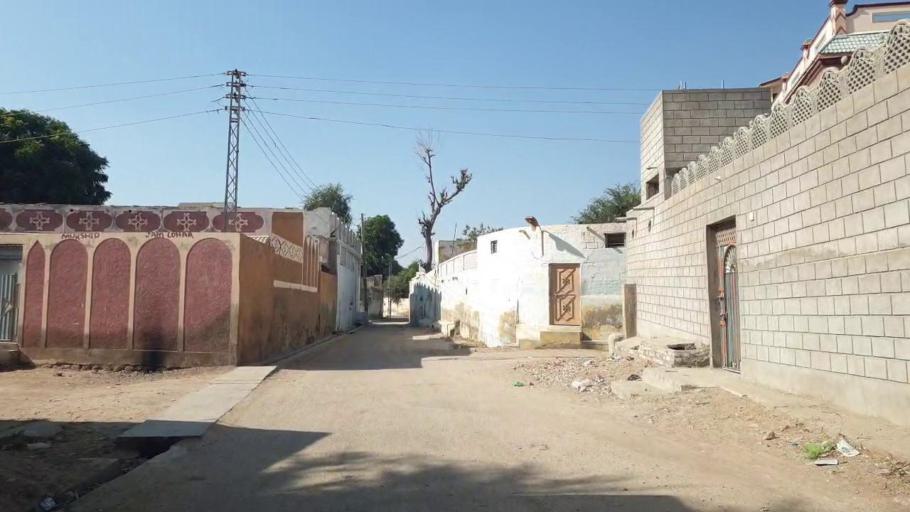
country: PK
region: Sindh
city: Jamshoro
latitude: 25.4107
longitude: 67.7840
